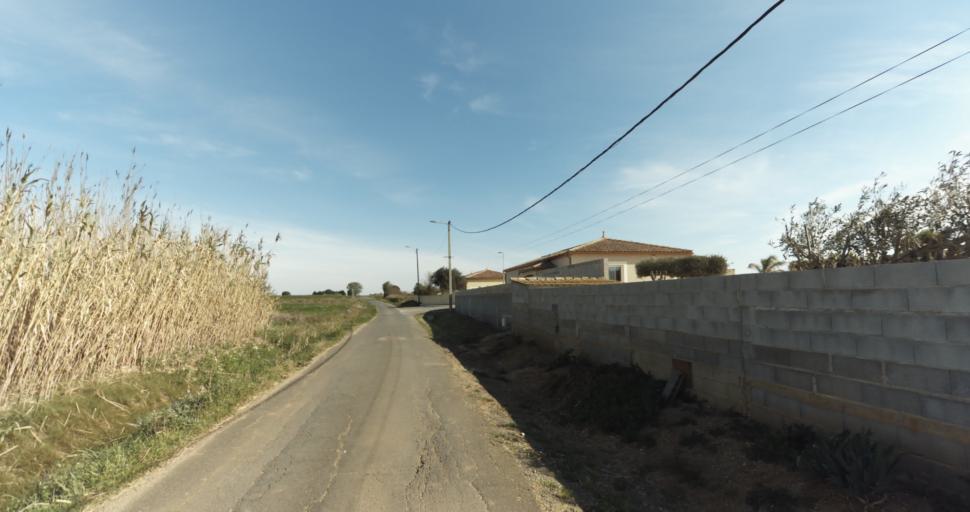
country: FR
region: Languedoc-Roussillon
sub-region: Departement de l'Herault
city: Marseillan
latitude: 43.3385
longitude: 3.5168
